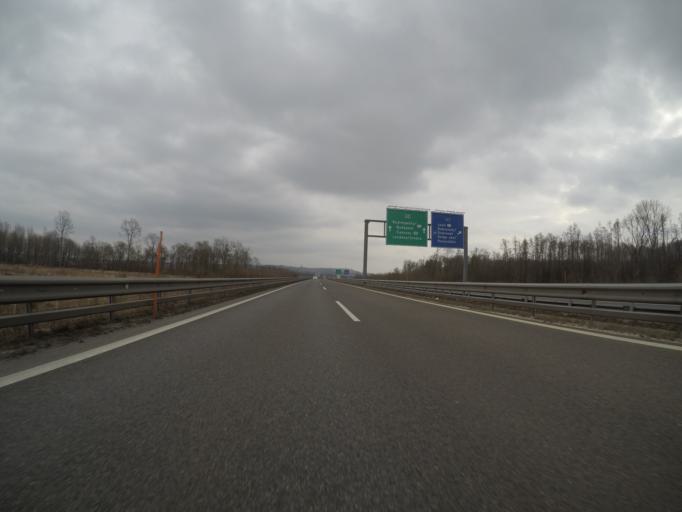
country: SI
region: Lendava-Lendva
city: Lendava
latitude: 46.5922
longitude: 16.4215
